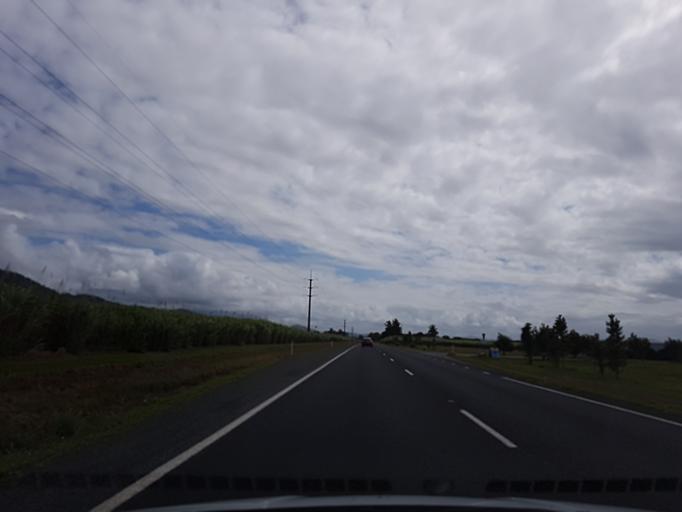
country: AU
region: Queensland
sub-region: Cairns
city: Port Douglas
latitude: -16.5173
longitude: 145.4481
